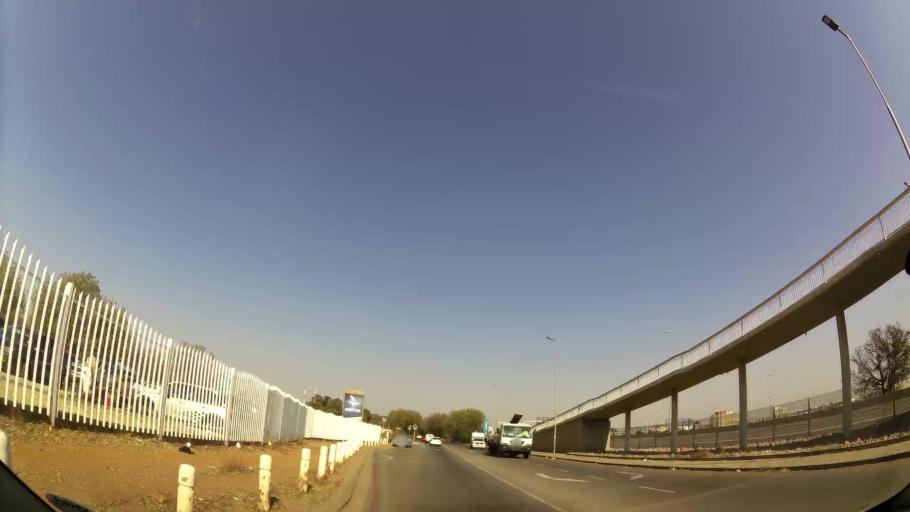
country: ZA
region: Gauteng
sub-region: City of Johannesburg Metropolitan Municipality
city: Modderfontein
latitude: -26.1370
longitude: 28.2231
